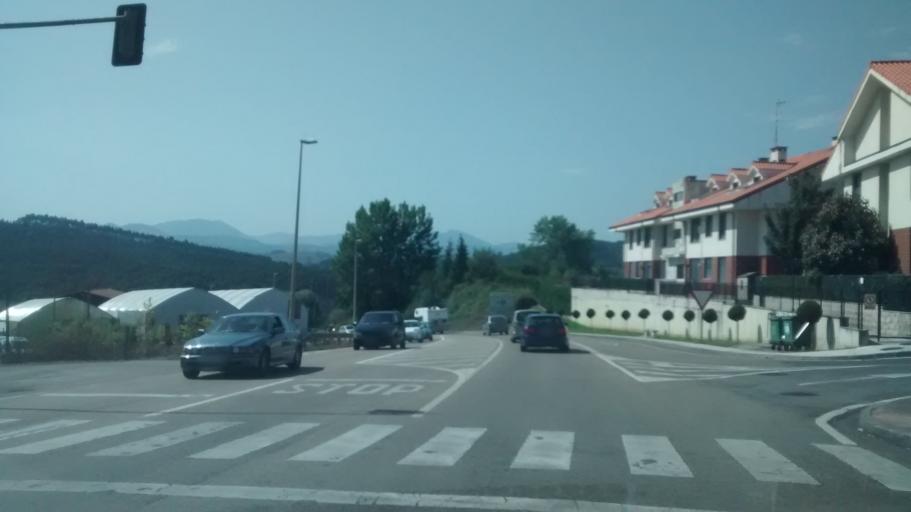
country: ES
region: Cantabria
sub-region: Provincia de Cantabria
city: San Miguel de Meruelo
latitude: 43.4454
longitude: -3.5658
